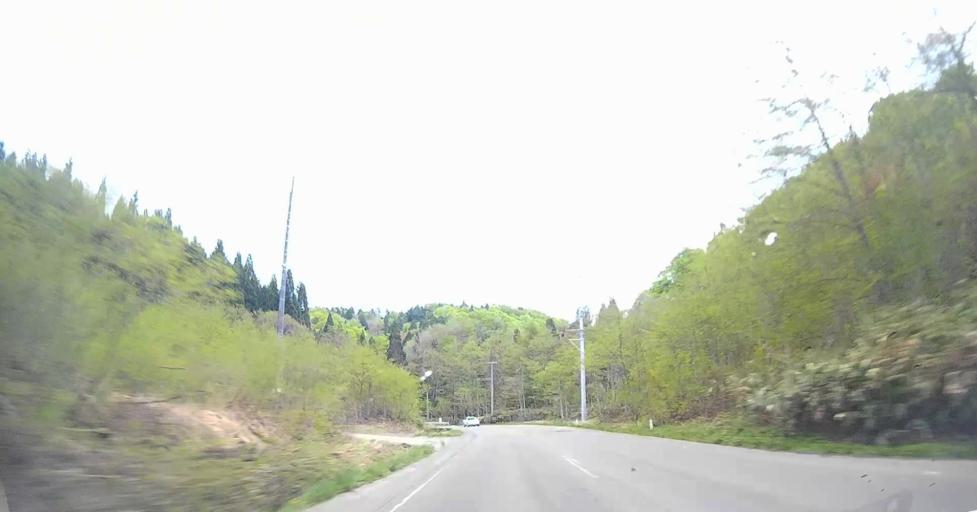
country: JP
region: Aomori
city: Goshogawara
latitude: 41.1146
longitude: 140.5289
